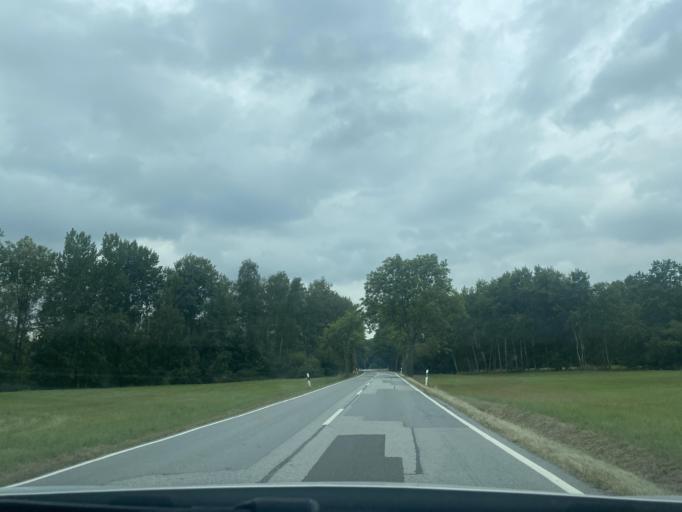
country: DE
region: Saxony
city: Guttau
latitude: 51.2714
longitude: 14.6183
